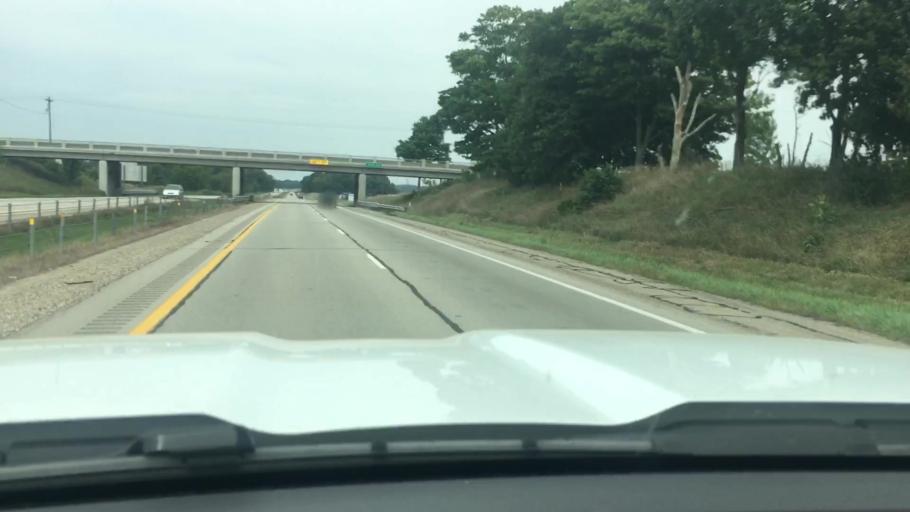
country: US
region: Michigan
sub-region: Allegan County
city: Wayland
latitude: 42.7383
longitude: -85.6732
